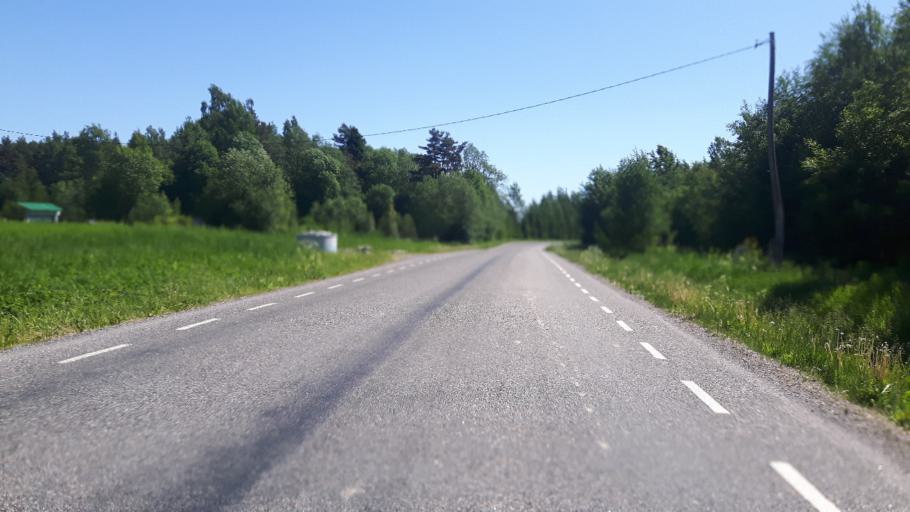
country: EE
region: Raplamaa
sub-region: Kohila vald
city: Kohila
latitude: 59.1798
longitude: 24.7260
